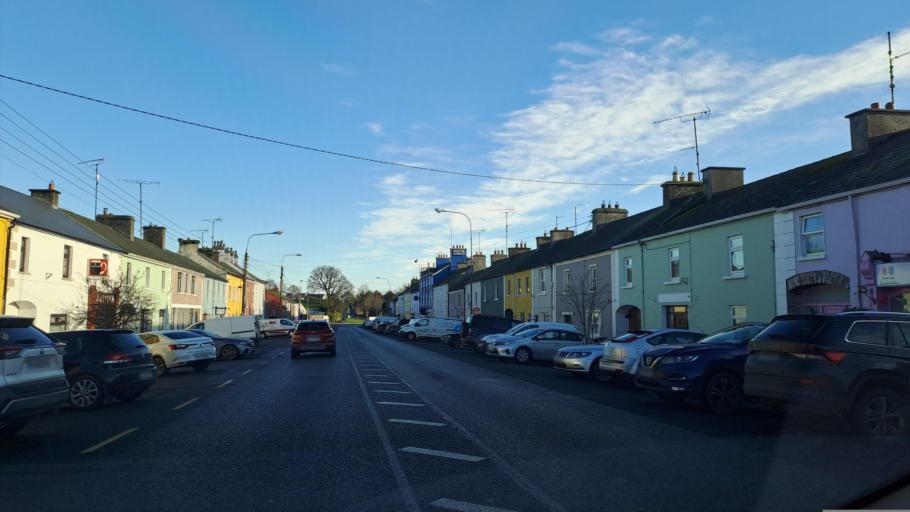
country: IE
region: Ulster
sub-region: An Cabhan
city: Mullagh
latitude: 53.8115
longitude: -6.9470
